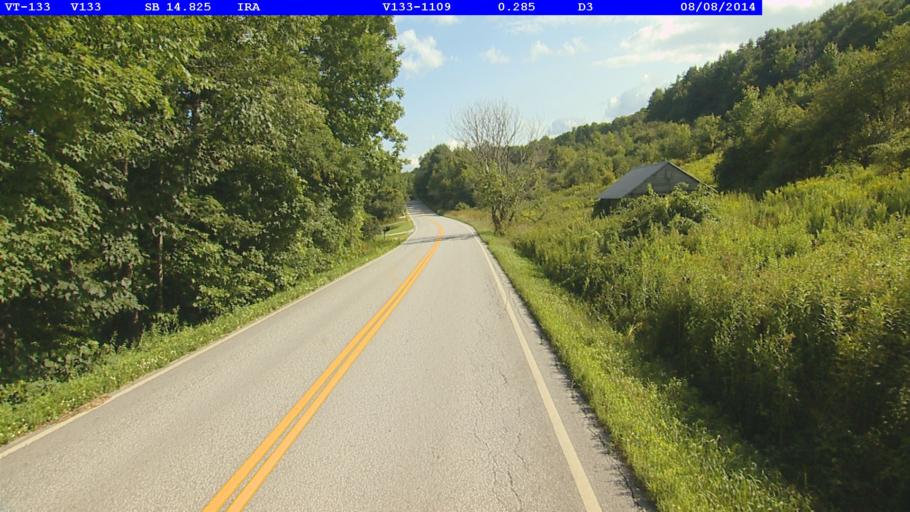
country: US
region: Vermont
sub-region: Rutland County
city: West Rutland
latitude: 43.4993
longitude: -73.0797
